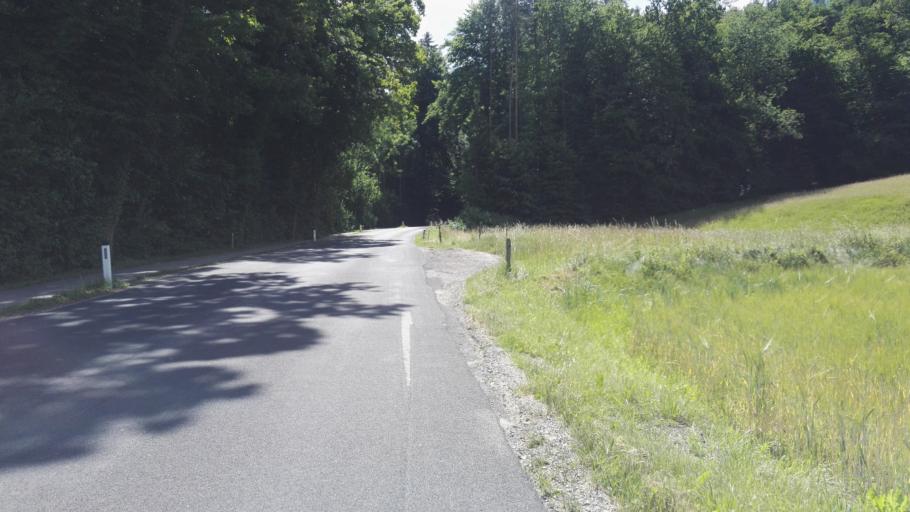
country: AT
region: Styria
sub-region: Politischer Bezirk Graz-Umgebung
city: Eggersdorf bei Graz
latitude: 47.0938
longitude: 15.5522
